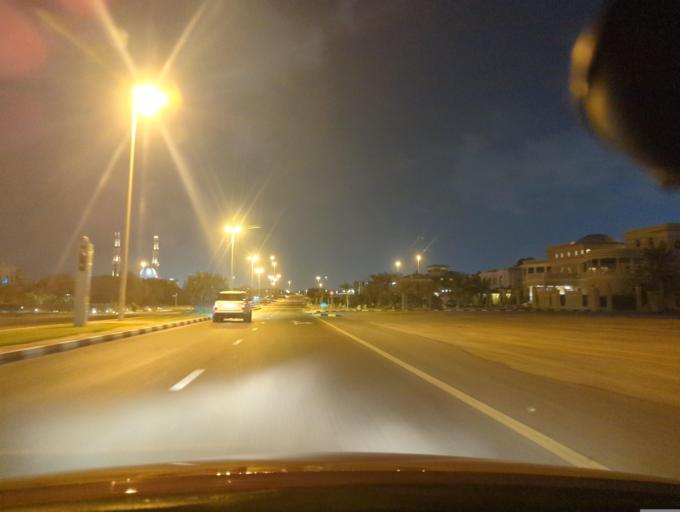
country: AE
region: Ash Shariqah
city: Sharjah
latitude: 25.3452
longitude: 55.4681
